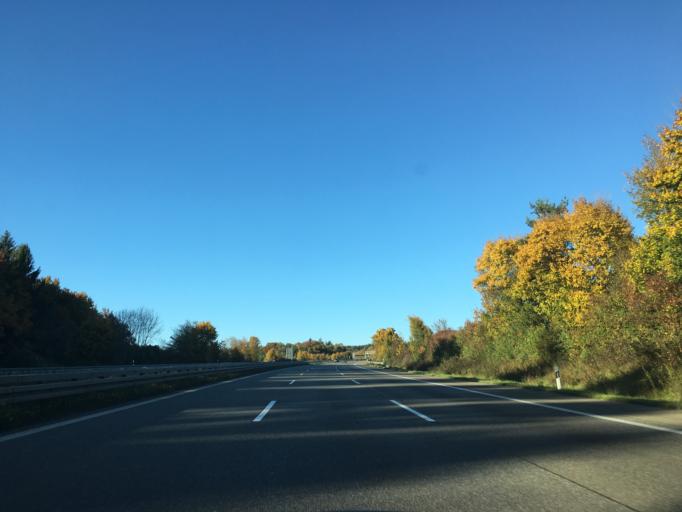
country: DE
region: Baden-Wuerttemberg
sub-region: Freiburg Region
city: Engen
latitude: 47.8756
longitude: 8.7762
